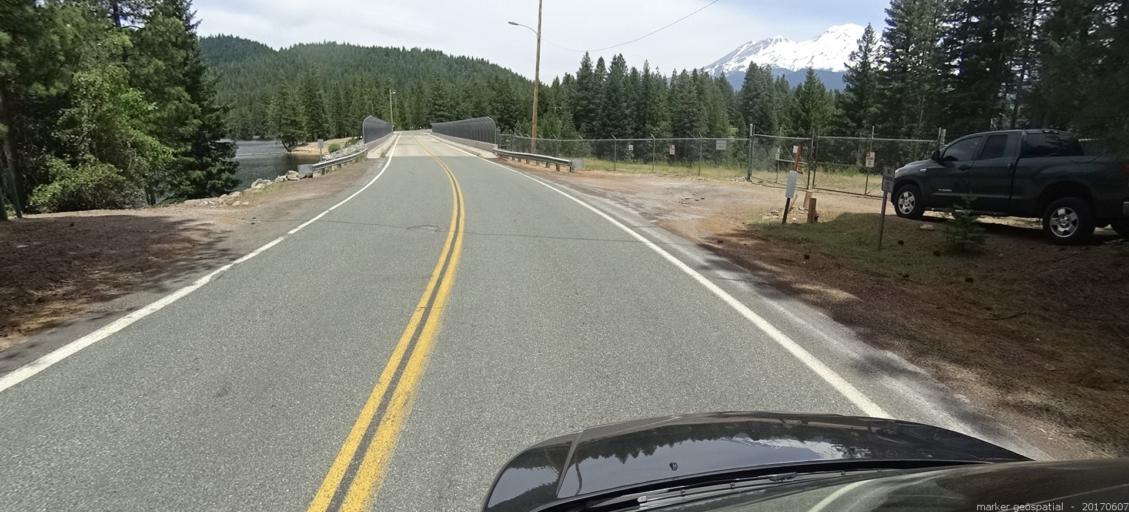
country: US
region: California
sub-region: Siskiyou County
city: Mount Shasta
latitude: 41.2779
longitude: -122.3289
